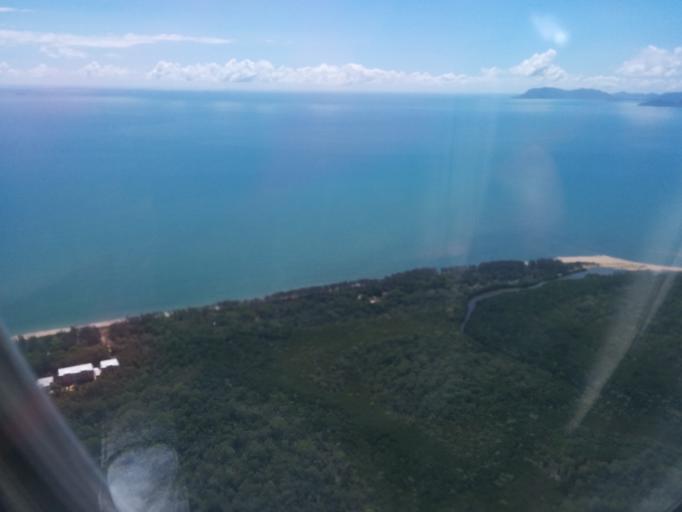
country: AU
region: Queensland
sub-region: Cairns
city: Yorkeys Knob
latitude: -16.8153
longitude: 145.7209
